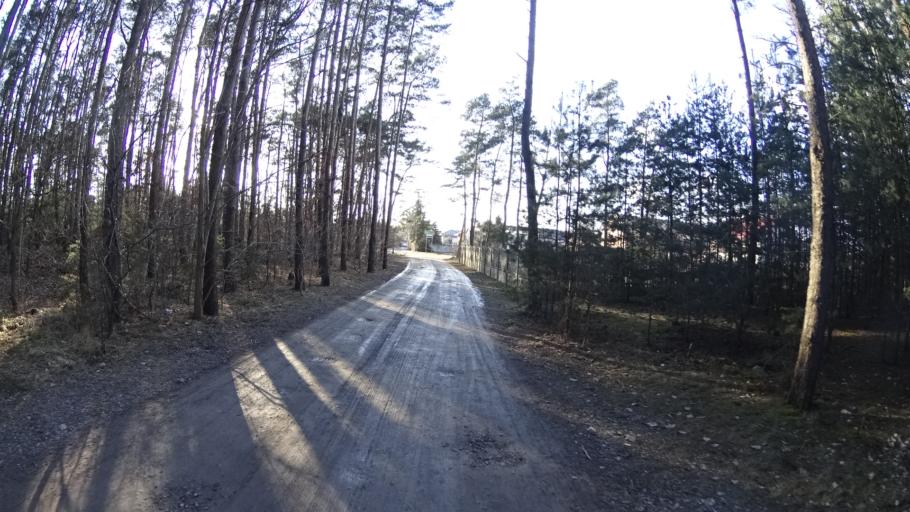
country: PL
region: Masovian Voivodeship
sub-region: Powiat warszawski zachodni
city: Hornowek
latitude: 52.2624
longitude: 20.7835
